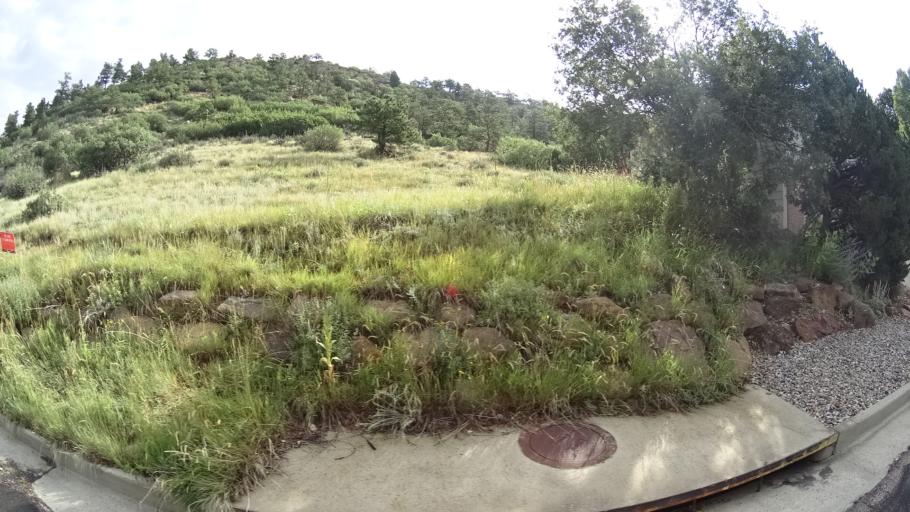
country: US
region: Colorado
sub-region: El Paso County
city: Manitou Springs
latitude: 38.9097
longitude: -104.8573
